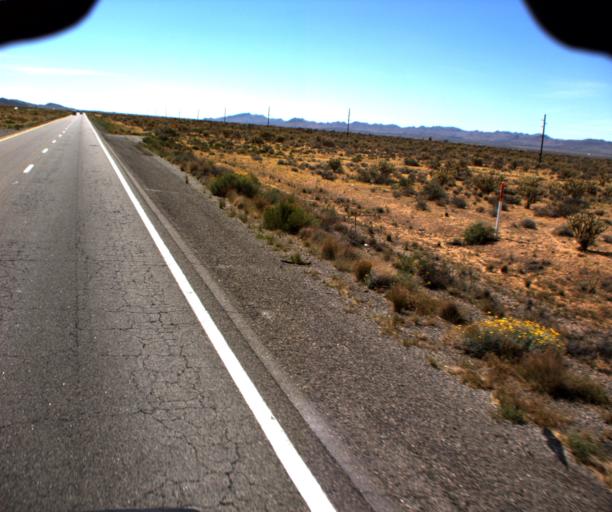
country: US
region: Arizona
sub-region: Mohave County
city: Dolan Springs
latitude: 35.5098
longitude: -114.3389
